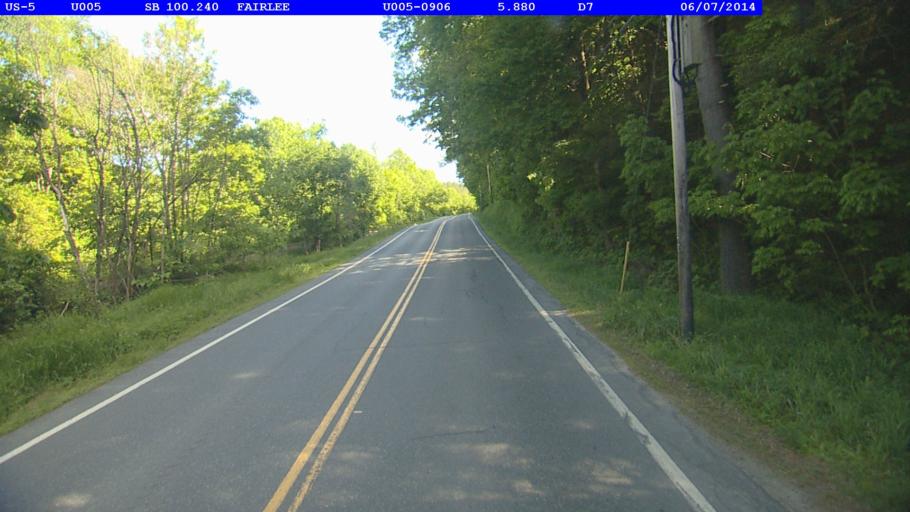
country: US
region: New Hampshire
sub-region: Grafton County
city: Orford
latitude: 43.9416
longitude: -72.1197
